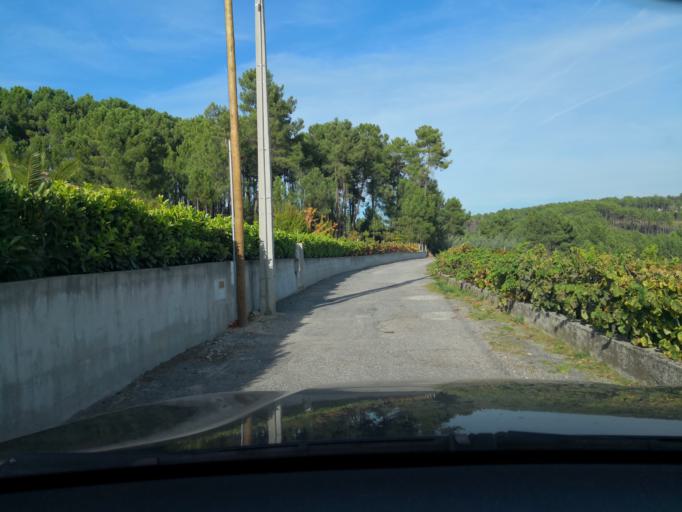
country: PT
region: Vila Real
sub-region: Vila Real
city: Vila Real
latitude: 41.3299
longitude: -7.7398
